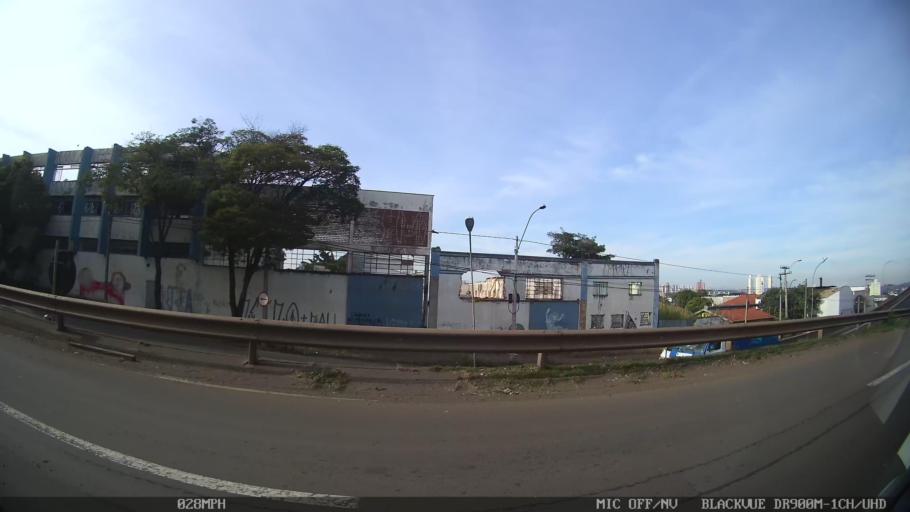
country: BR
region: Sao Paulo
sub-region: Piracicaba
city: Piracicaba
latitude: -22.7011
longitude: -47.6566
